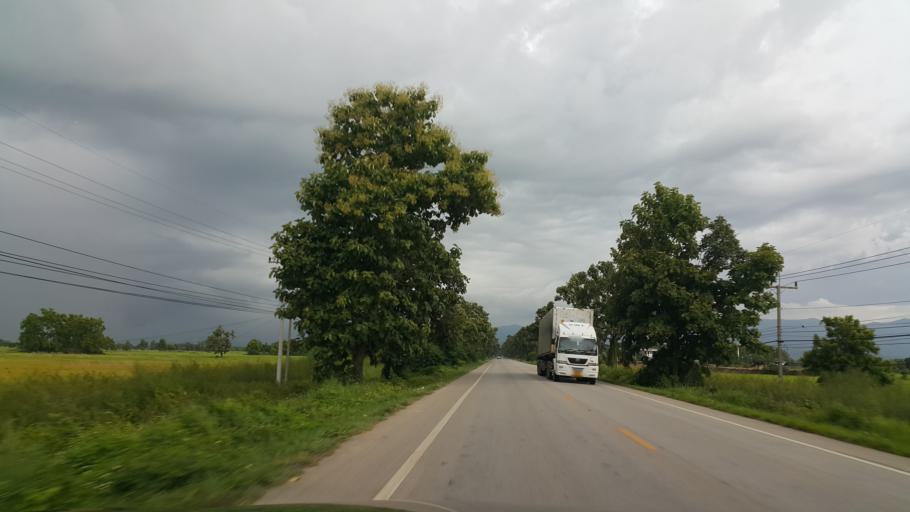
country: TH
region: Phayao
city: Dok Kham Tai
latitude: 19.1871
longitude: 100.0196
